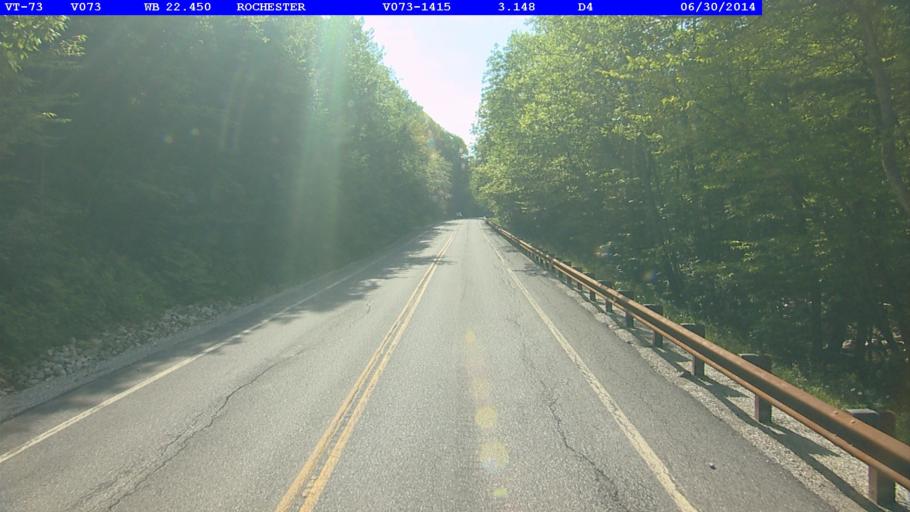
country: US
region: Vermont
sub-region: Rutland County
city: Brandon
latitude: 43.8530
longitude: -72.9079
